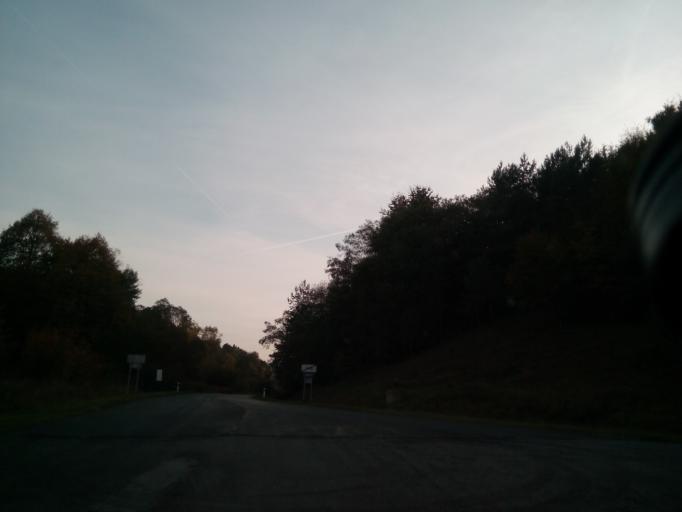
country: SK
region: Presovsky
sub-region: Okres Bardejov
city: Bardejov
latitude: 49.3588
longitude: 21.3967
